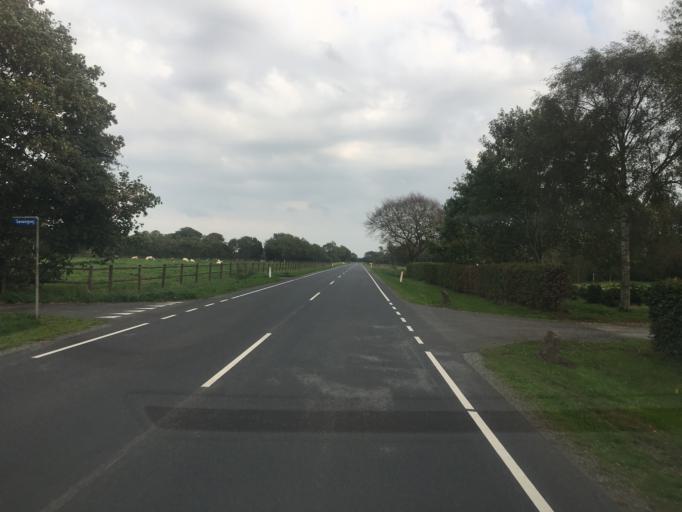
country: DK
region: South Denmark
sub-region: Tonder Kommune
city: Logumkloster
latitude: 54.9778
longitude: 9.0365
